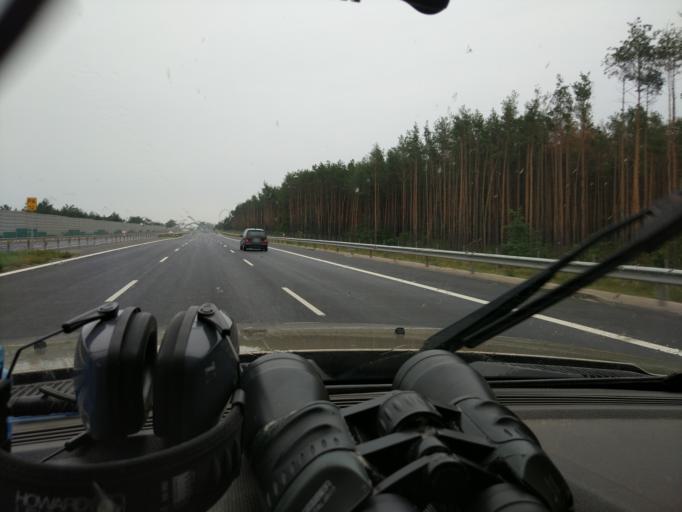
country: PL
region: Masovian Voivodeship
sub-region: Powiat wolominski
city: Radzymin
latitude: 52.3843
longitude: 21.1923
